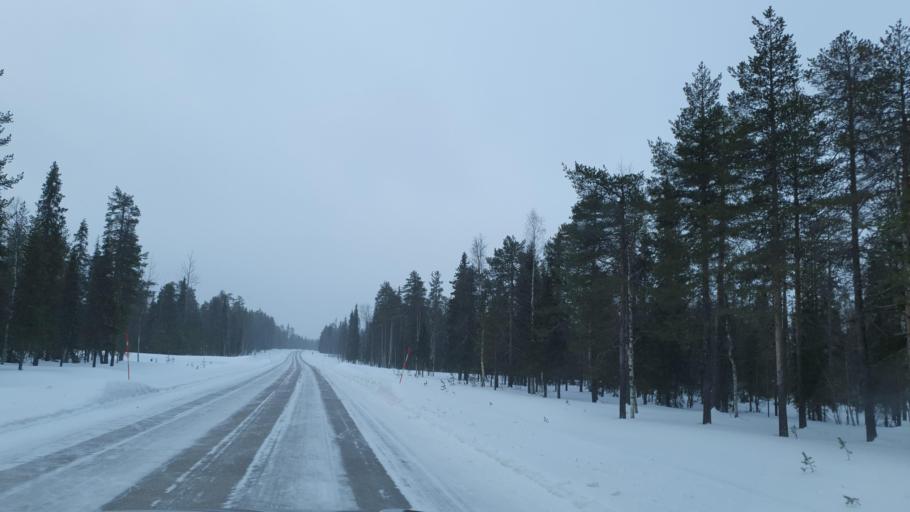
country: FI
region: Lapland
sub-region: Tunturi-Lappi
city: Kolari
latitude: 67.4700
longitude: 23.8634
